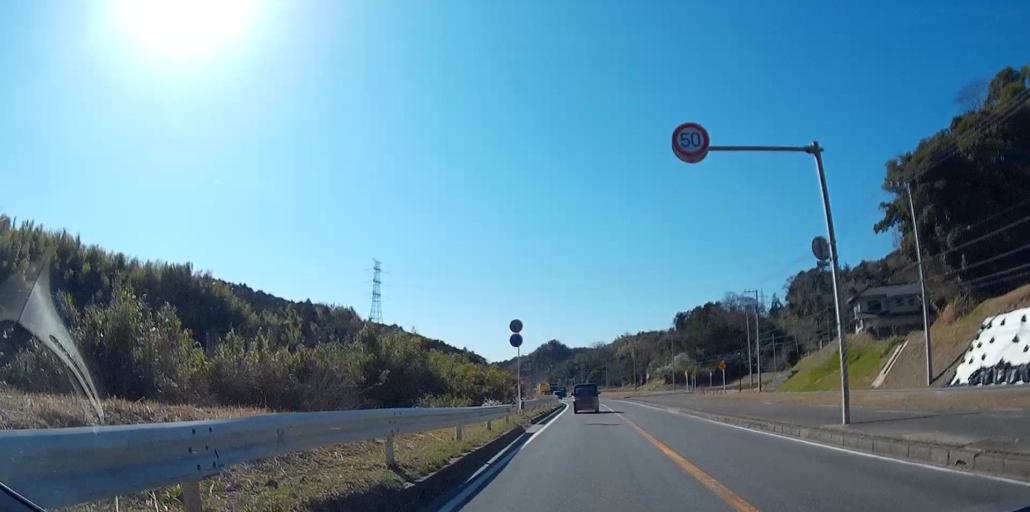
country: JP
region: Chiba
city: Kimitsu
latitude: 35.2887
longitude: 139.9153
